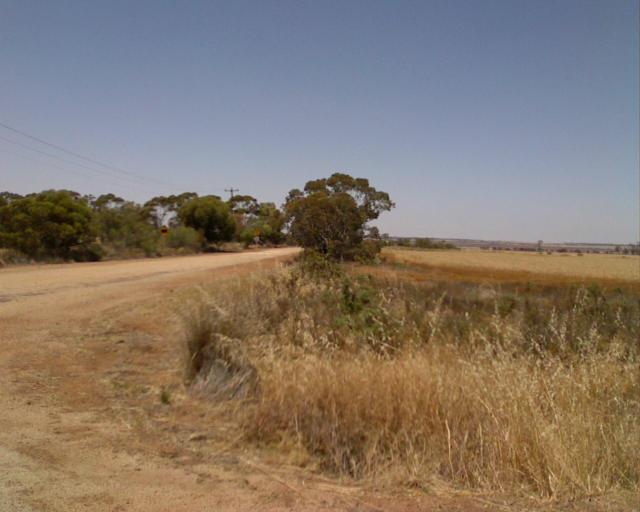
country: AU
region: Western Australia
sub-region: Wongan-Ballidu
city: Wongan Hills
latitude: -30.4517
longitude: 117.5256
